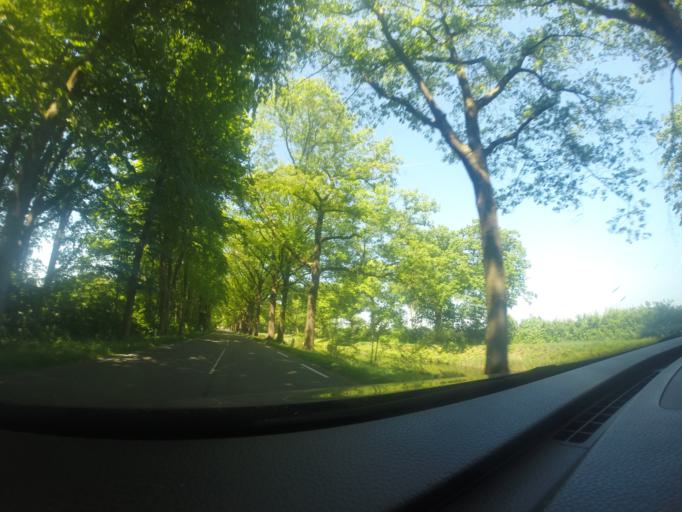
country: NL
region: Gelderland
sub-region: Gemeente Brummen
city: Eerbeek
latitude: 52.1074
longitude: 6.0841
